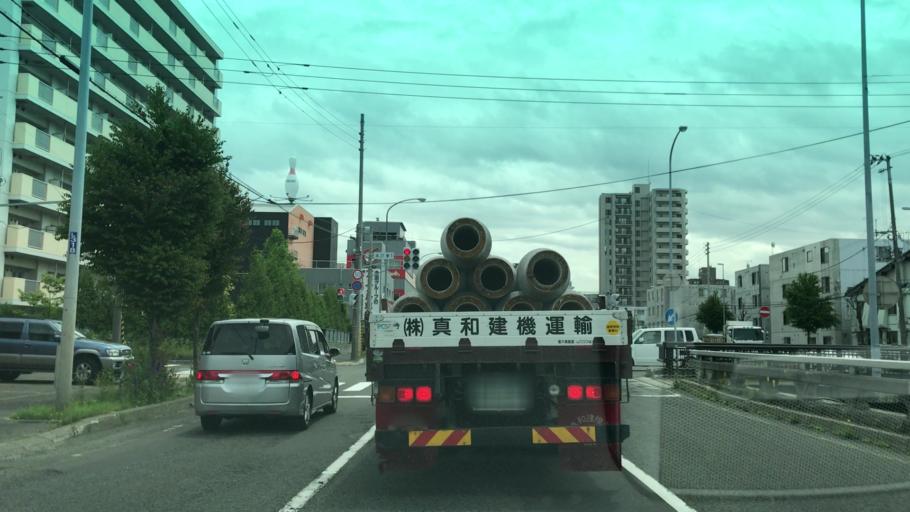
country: JP
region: Hokkaido
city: Sapporo
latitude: 43.0881
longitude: 141.3485
